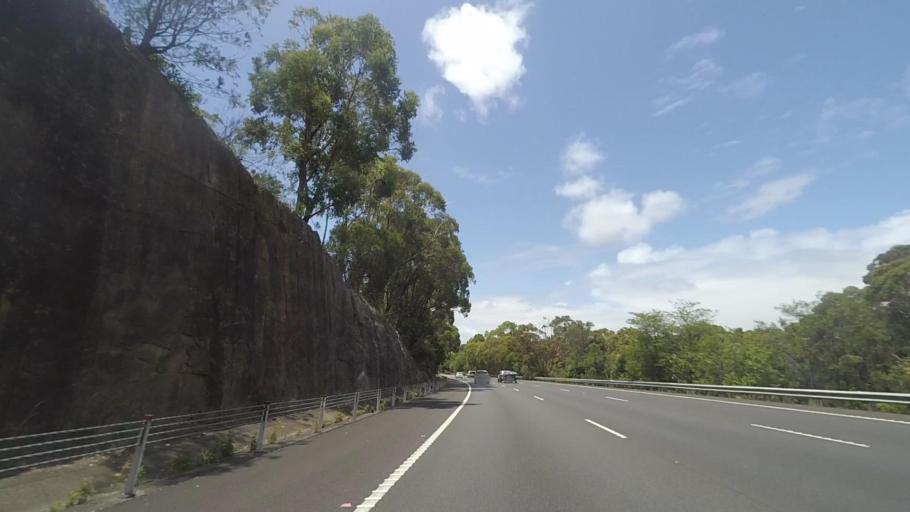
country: AU
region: New South Wales
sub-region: Gosford Shire
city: Lisarow
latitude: -33.3652
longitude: 151.3323
